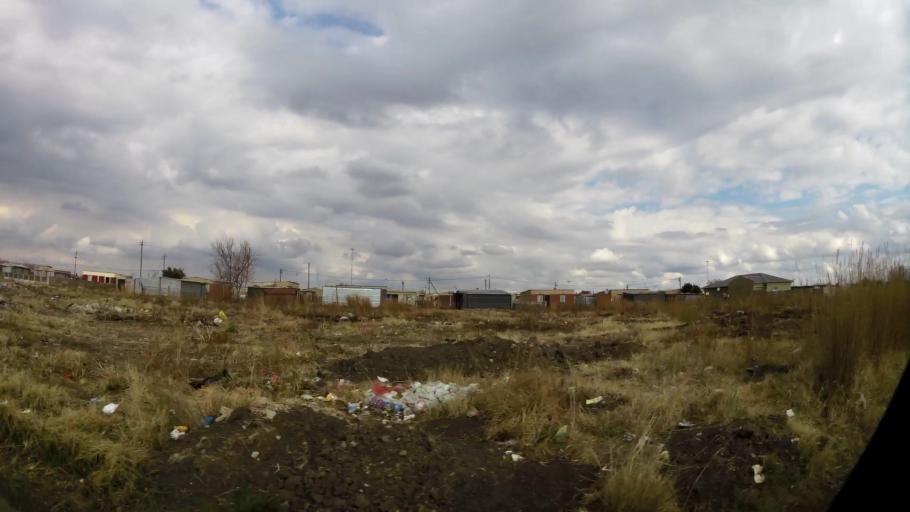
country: ZA
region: Gauteng
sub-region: Sedibeng District Municipality
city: Vanderbijlpark
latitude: -26.6820
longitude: 27.7836
